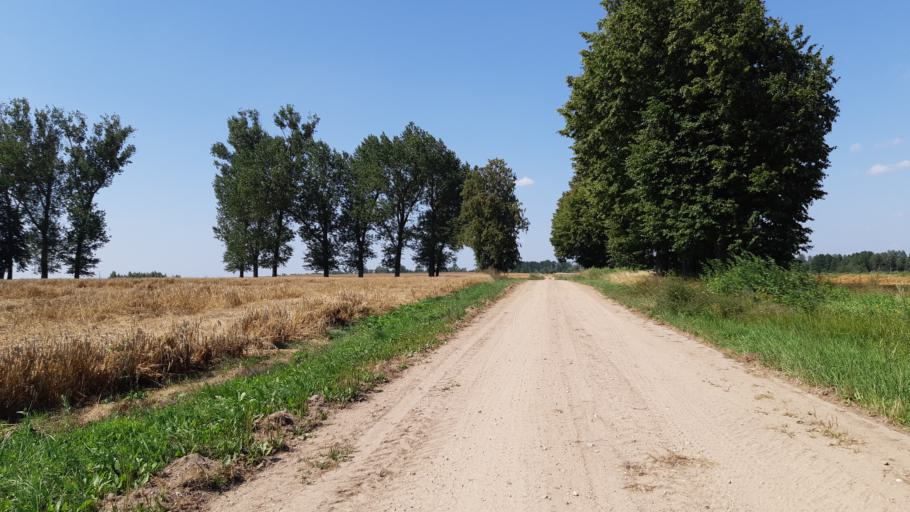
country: LT
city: Virbalis
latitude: 54.6389
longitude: 22.8221
